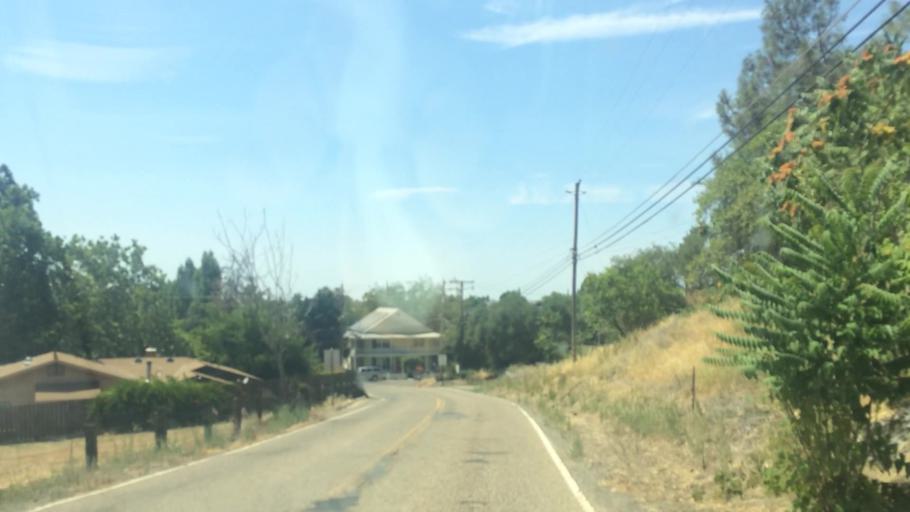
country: US
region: California
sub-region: Amador County
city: Sutter Creek
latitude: 38.3822
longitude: -120.7987
